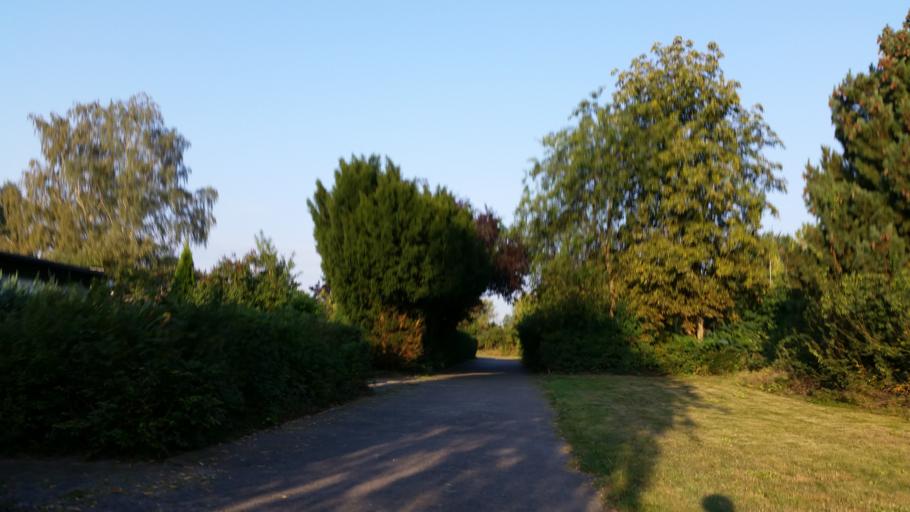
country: DE
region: Berlin
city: Marienfelde
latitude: 52.3983
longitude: 13.3624
